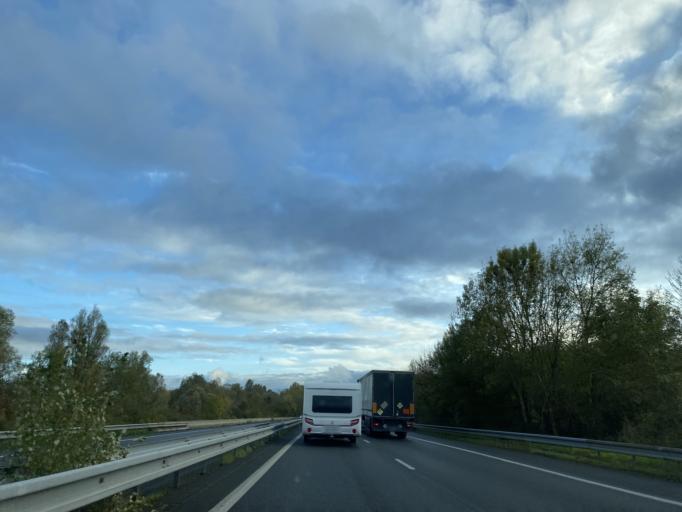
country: FR
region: Centre
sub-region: Departement du Cher
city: Foecy
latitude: 47.1747
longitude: 2.1784
